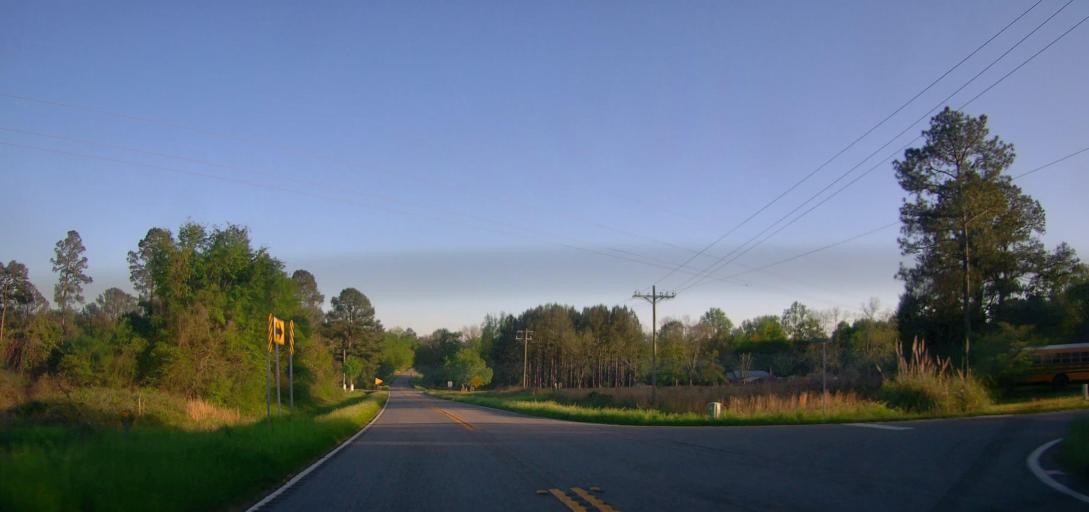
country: US
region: Georgia
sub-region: Marion County
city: Buena Vista
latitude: 32.3871
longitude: -84.4428
